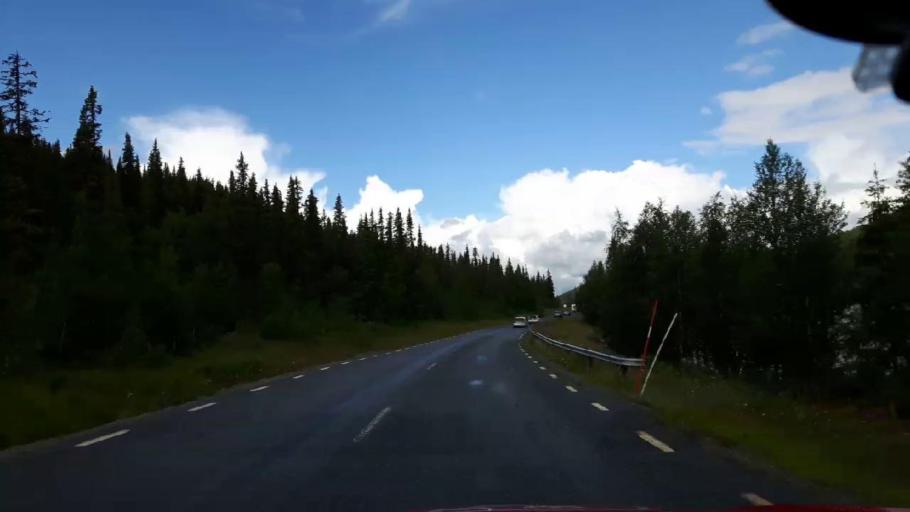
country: SE
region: Vaesterbotten
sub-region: Vilhelmina Kommun
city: Sjoberg
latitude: 65.0233
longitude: 15.1554
